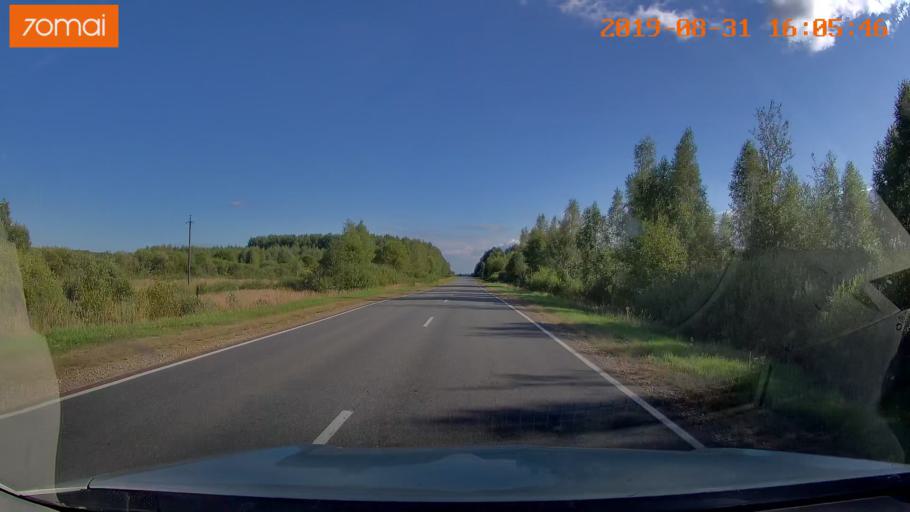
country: RU
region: Kaluga
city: Yukhnov
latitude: 54.6341
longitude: 35.3383
